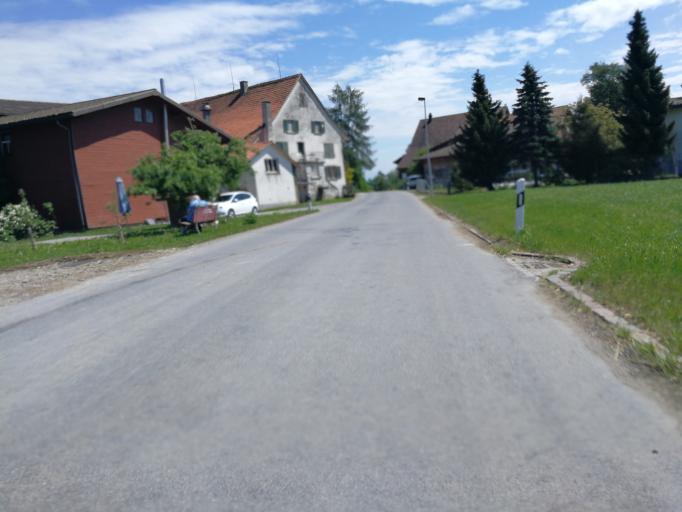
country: CH
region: Zurich
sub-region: Bezirk Uster
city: Esslingen
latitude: 47.2828
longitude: 8.6991
